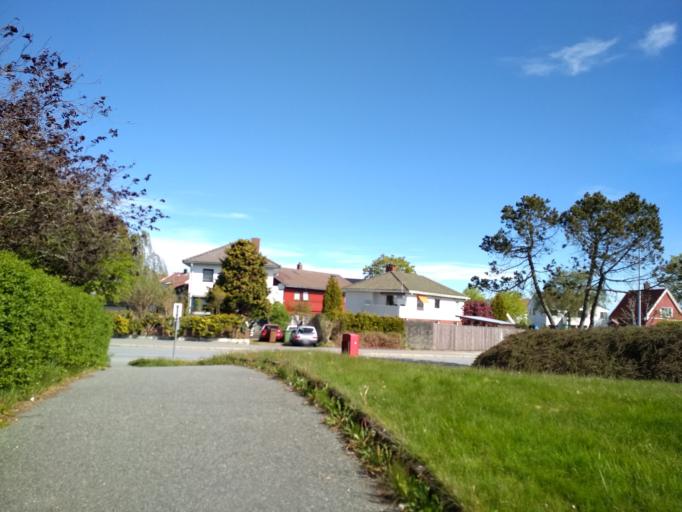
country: NO
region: Rogaland
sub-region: Stavanger
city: Stavanger
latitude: 58.9538
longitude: 5.7376
